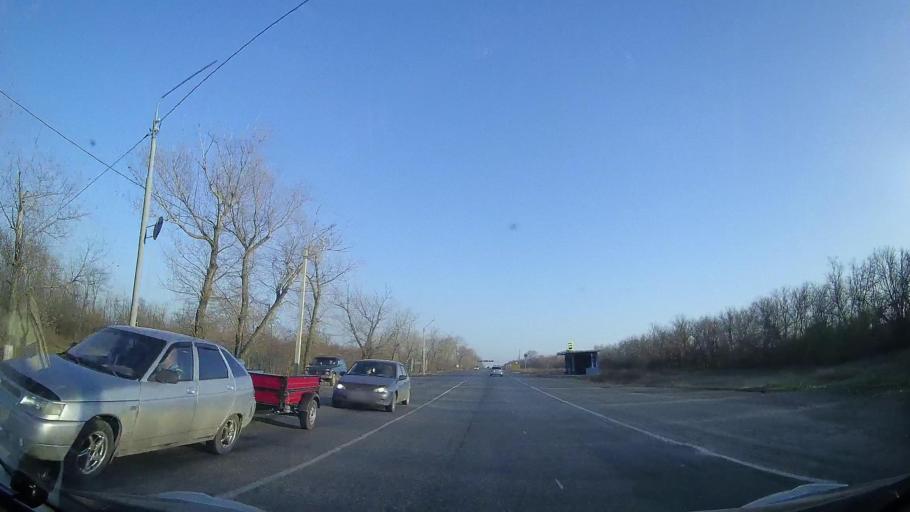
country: RU
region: Rostov
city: Bataysk
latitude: 47.0808
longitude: 39.7745
